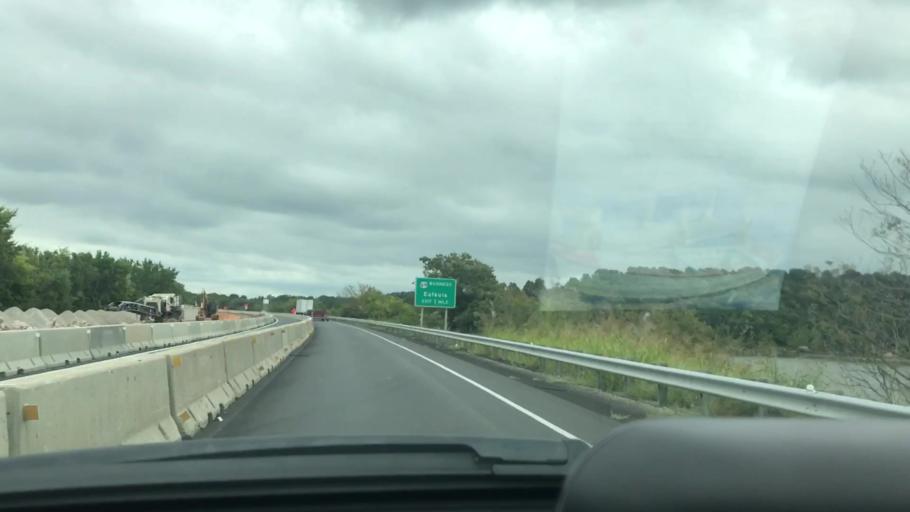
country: US
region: Oklahoma
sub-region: McIntosh County
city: Eufaula
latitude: 35.2450
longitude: -95.5855
